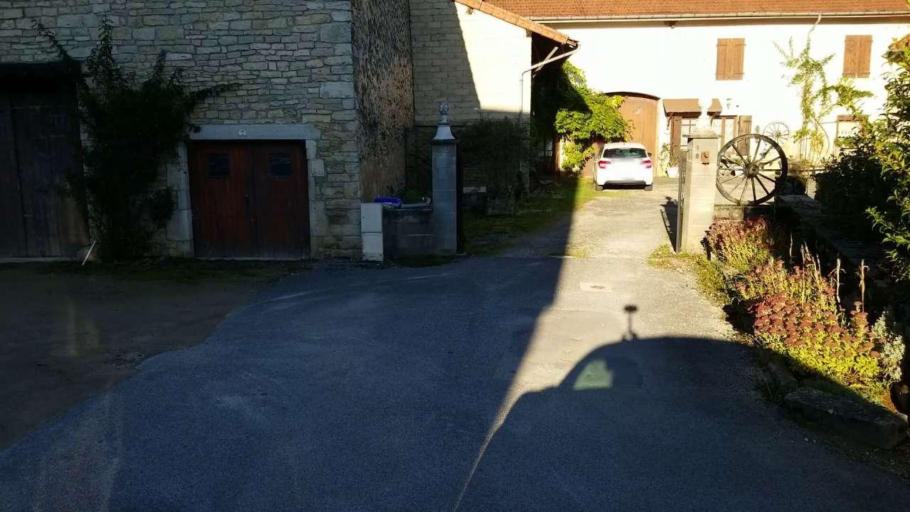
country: FR
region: Franche-Comte
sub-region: Departement du Jura
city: Perrigny
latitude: 46.6863
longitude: 5.6588
